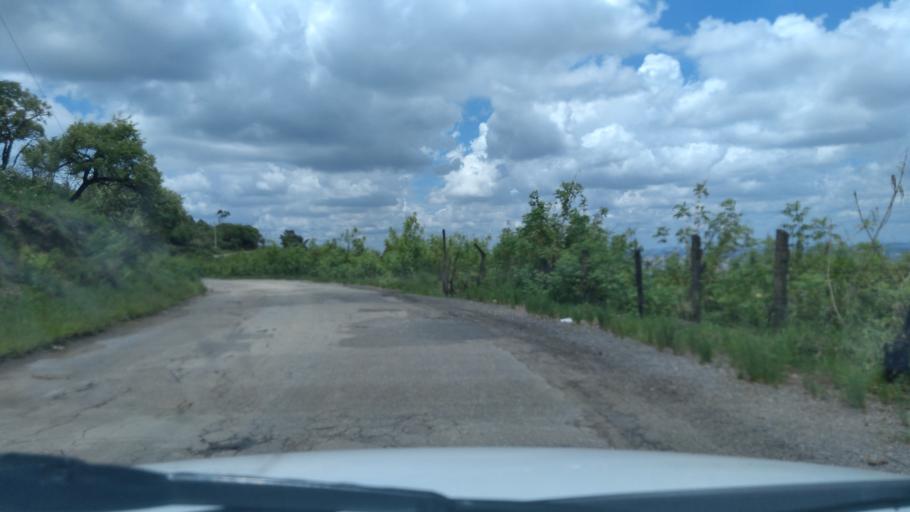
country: BR
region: Minas Gerais
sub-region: Belo Horizonte
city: Belo Horizonte
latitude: -19.9240
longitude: -43.8772
